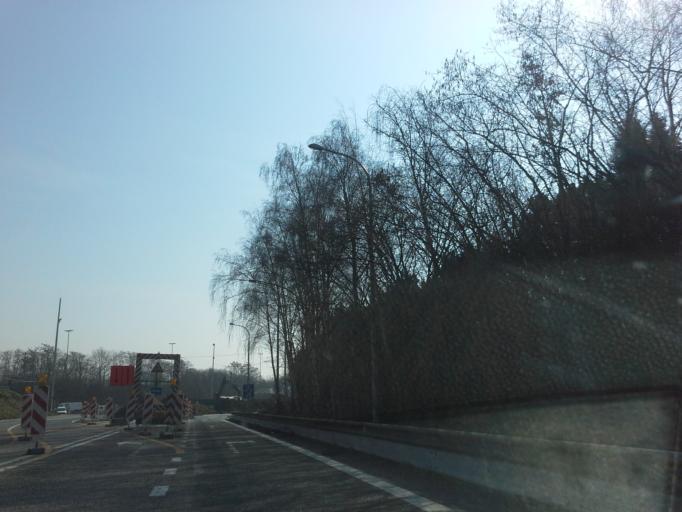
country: BE
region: Flanders
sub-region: Provincie Limburg
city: Hoeselt
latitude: 50.8585
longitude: 5.4970
